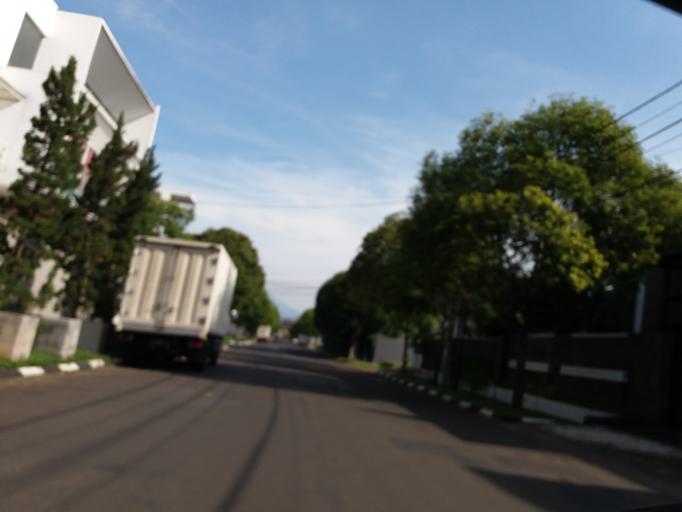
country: ID
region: West Java
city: Bandung
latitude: -6.9573
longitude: 107.6339
